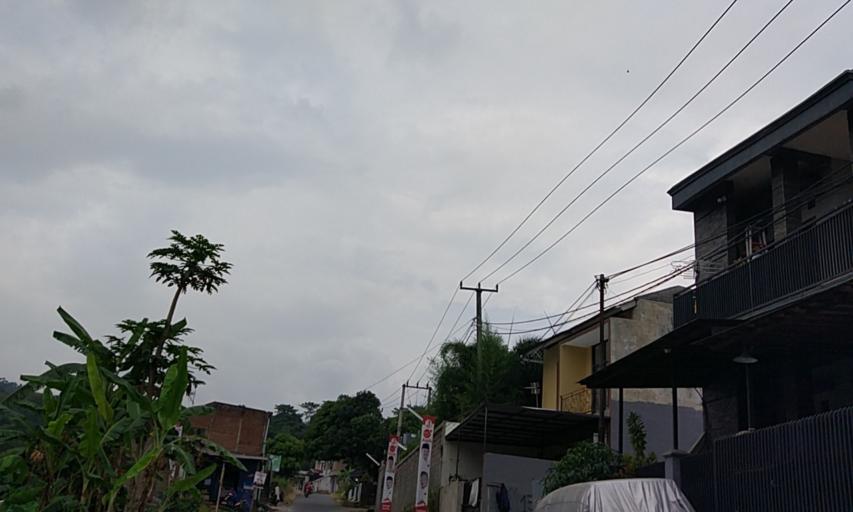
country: ID
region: West Java
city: Bandung
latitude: -6.8824
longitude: 107.6890
